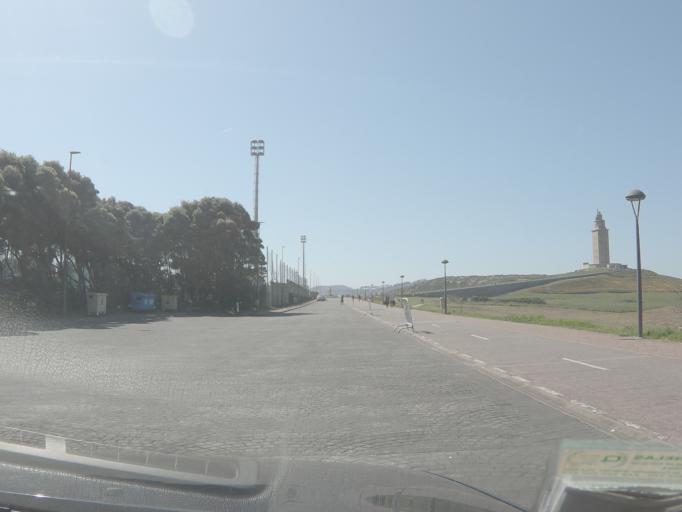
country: ES
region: Galicia
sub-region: Provincia da Coruna
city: A Coruna
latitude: 43.3861
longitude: -8.3993
